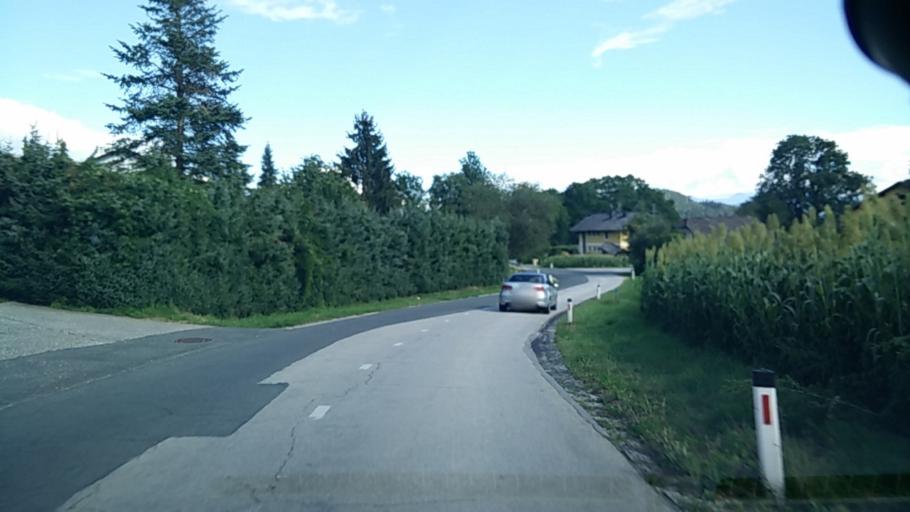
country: AT
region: Carinthia
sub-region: Politischer Bezirk Klagenfurt Land
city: Maria Saal
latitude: 46.7051
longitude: 14.4089
